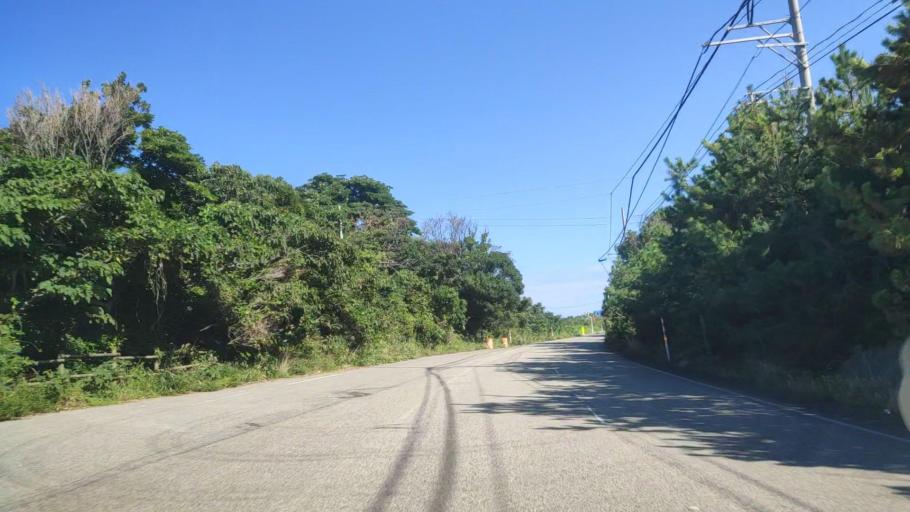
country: JP
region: Ishikawa
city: Hakui
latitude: 37.0705
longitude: 136.7213
